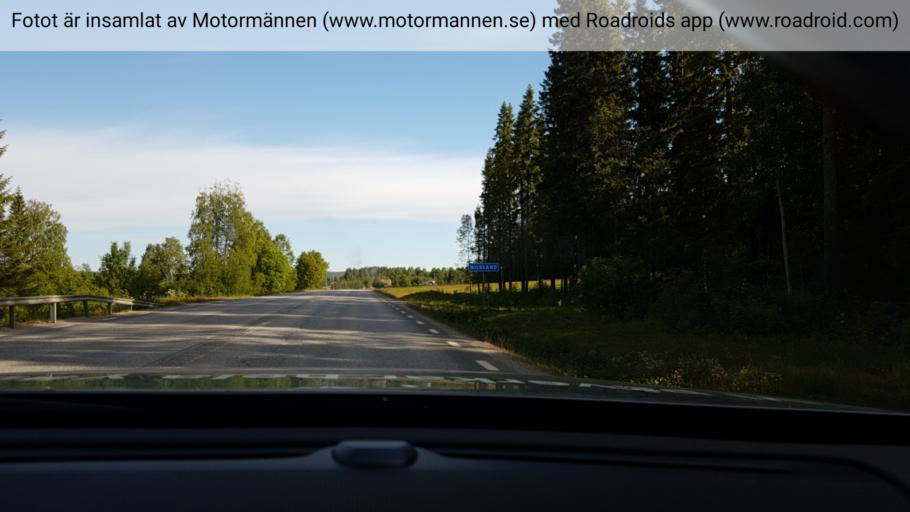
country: SE
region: Vaesterbotten
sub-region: Vannas Kommun
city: Vaennaes
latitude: 63.9780
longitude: 19.7312
